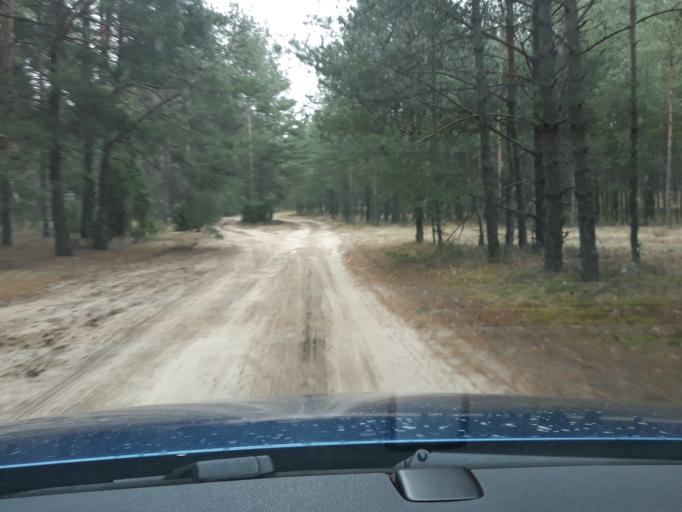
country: PL
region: Pomeranian Voivodeship
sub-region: Powiat chojnicki
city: Chojnice
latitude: 53.8619
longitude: 17.5476
